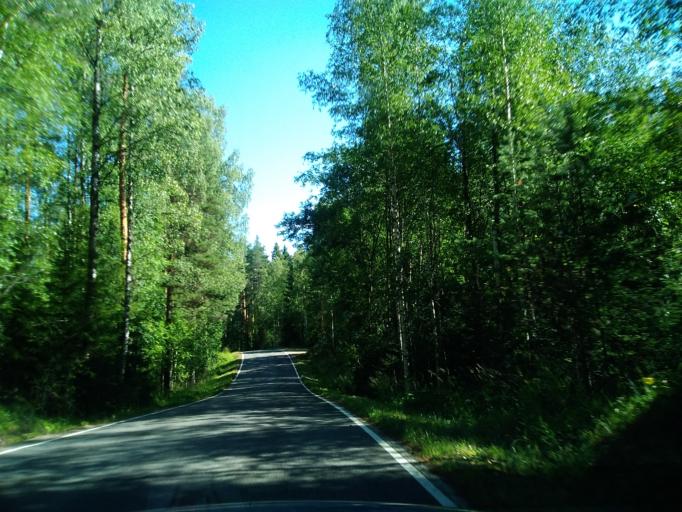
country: FI
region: Uusimaa
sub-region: Helsinki
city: Kaerkoelae
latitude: 60.7840
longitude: 24.0799
